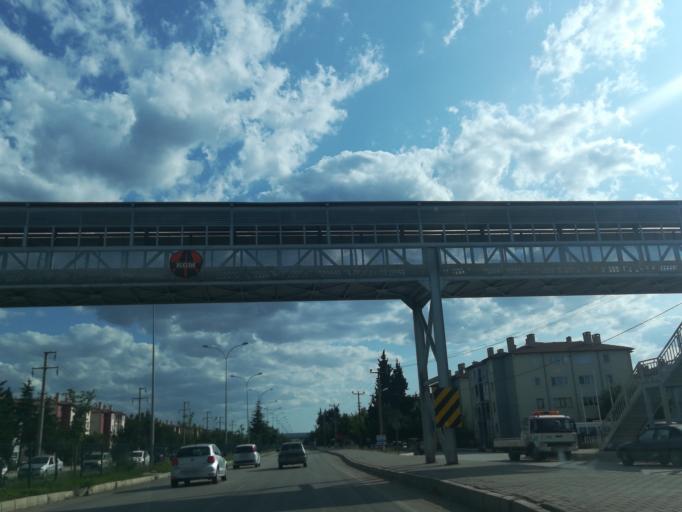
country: TR
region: Afyonkarahisar
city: Dinar
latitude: 38.0643
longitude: 30.1648
